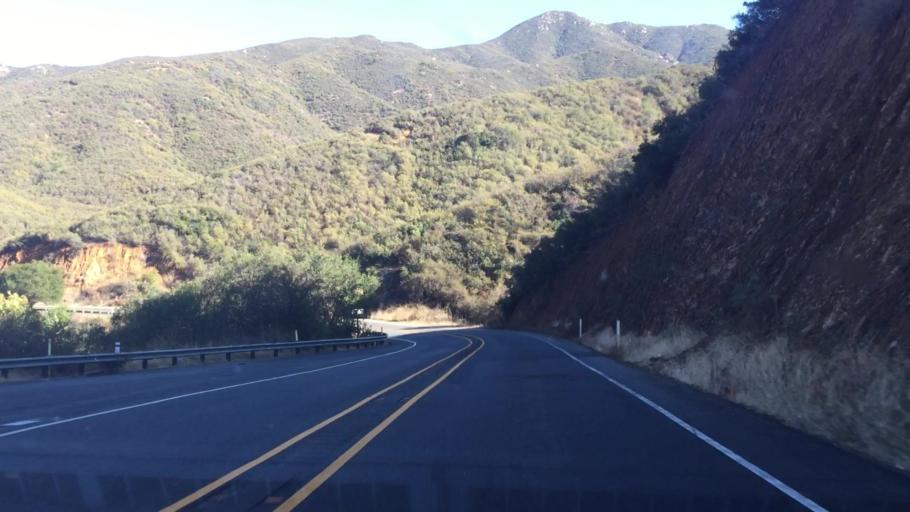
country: US
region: California
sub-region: Orange County
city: Coto De Caza
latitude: 33.5933
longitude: -117.4670
